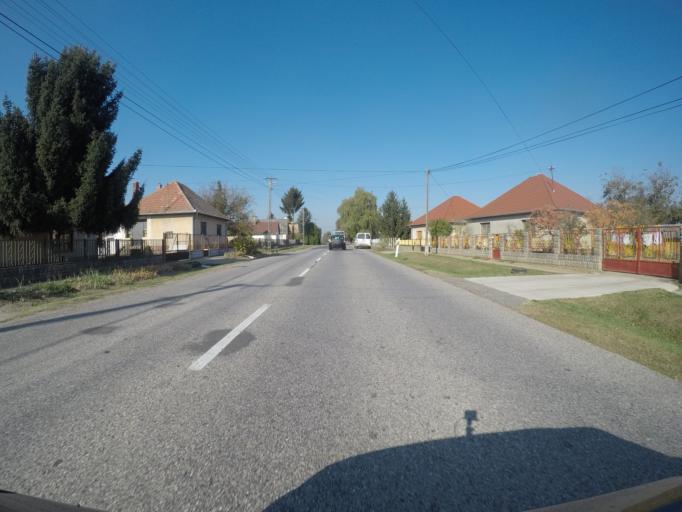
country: HU
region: Tolna
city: Szedres
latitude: 46.4857
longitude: 18.6809
